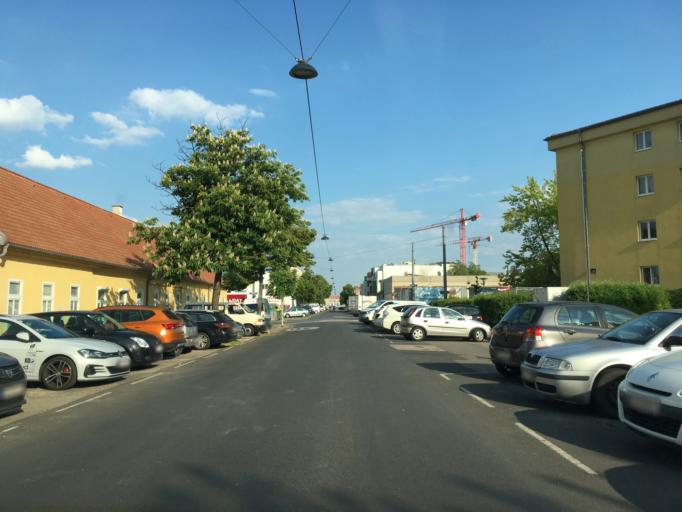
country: AT
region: Lower Austria
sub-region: Politischer Bezirk Modling
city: Vosendorf
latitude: 48.1398
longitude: 16.3200
